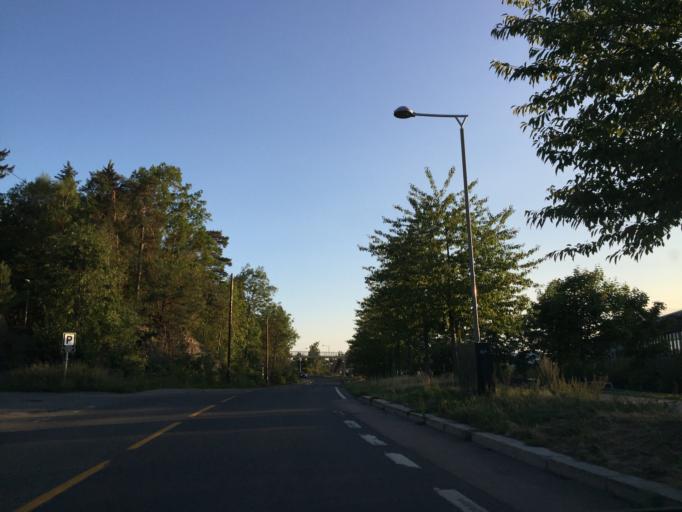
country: NO
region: Akershus
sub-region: Baerum
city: Lysaker
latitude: 59.8897
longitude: 10.6223
